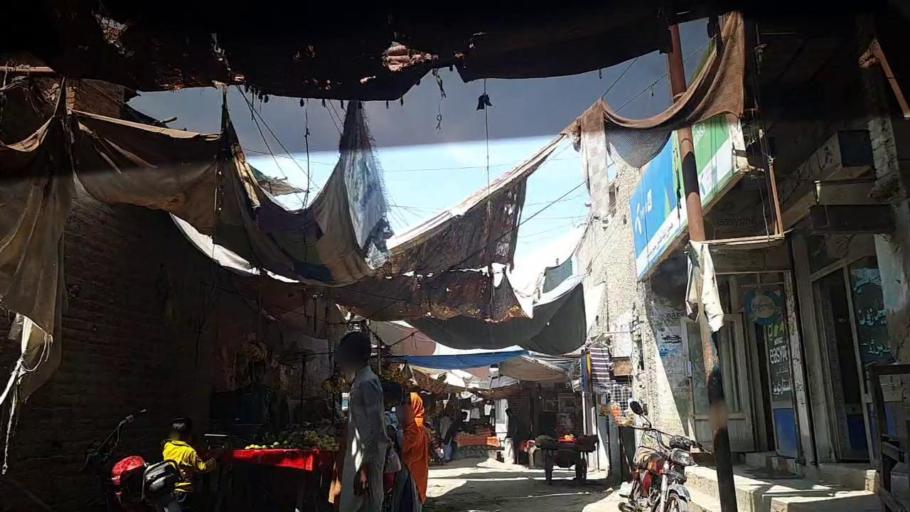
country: PK
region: Sindh
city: Thul
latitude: 28.1808
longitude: 68.7257
